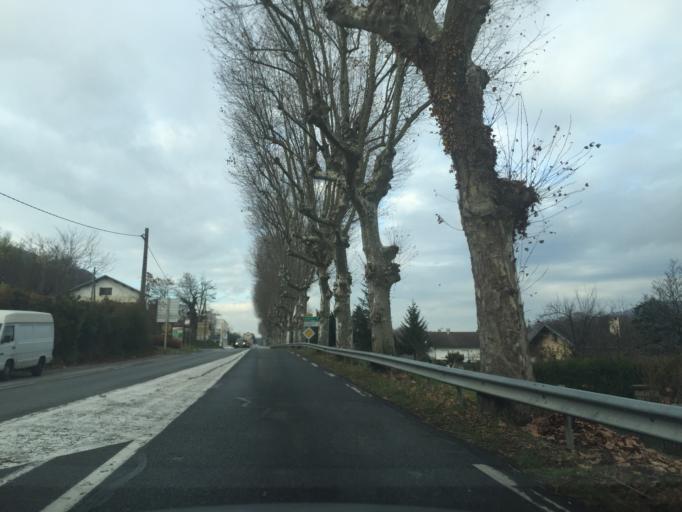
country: FR
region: Rhone-Alpes
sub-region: Departement de la Savoie
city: Gresy-sur-Aix
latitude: 45.7162
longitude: 5.9176
